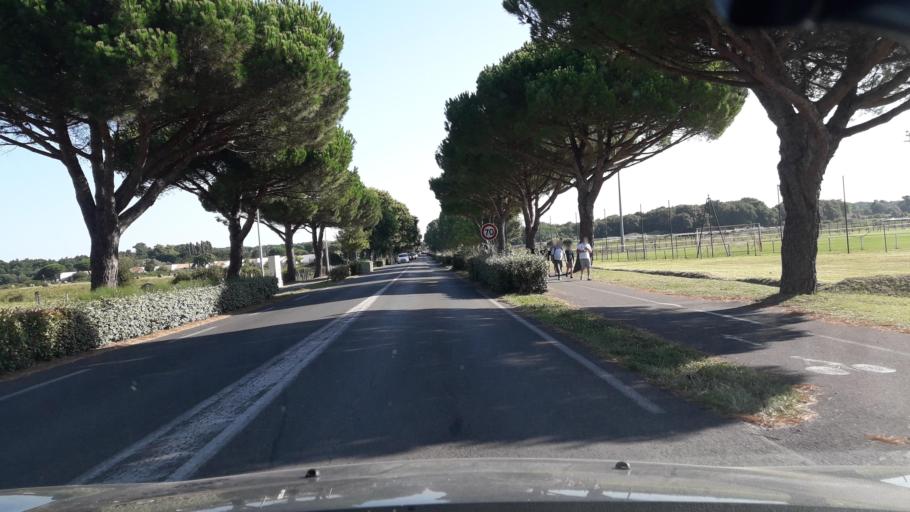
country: FR
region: Poitou-Charentes
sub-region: Departement de la Charente-Maritime
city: Les Mathes
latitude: 45.6957
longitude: -1.1758
